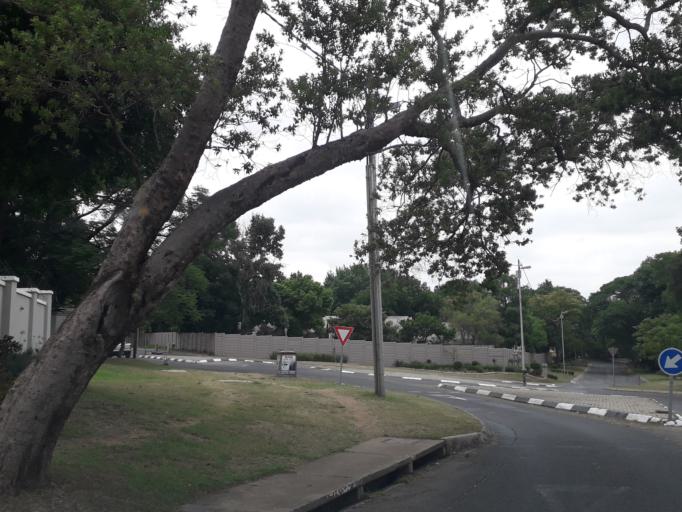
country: ZA
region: Gauteng
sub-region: City of Johannesburg Metropolitan Municipality
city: Midrand
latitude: -26.0453
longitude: 28.0431
